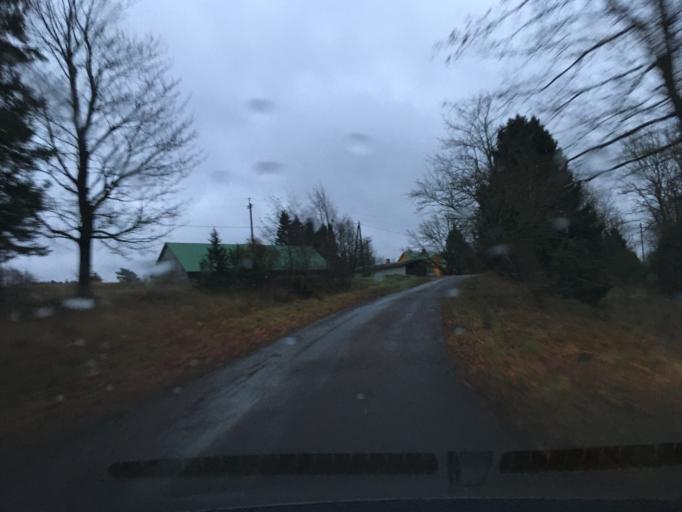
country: EE
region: Laeaene
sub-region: Lihula vald
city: Lihula
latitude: 58.5780
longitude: 23.7378
